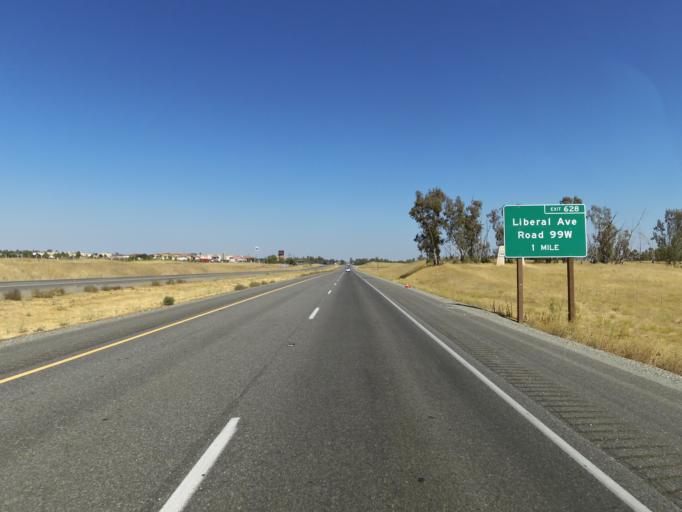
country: US
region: California
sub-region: Tehama County
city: Corning
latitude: 39.8669
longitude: -122.1999
